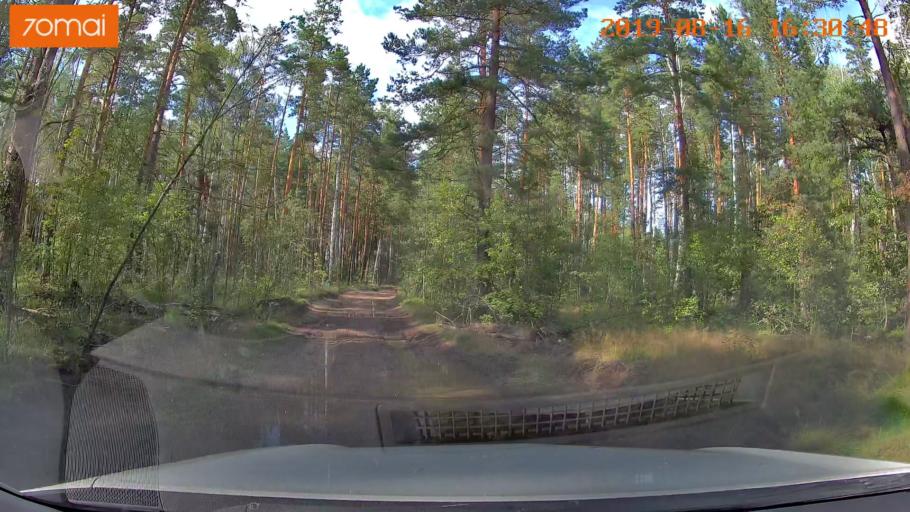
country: BY
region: Mogilev
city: Asipovichy
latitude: 53.2261
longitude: 28.7733
